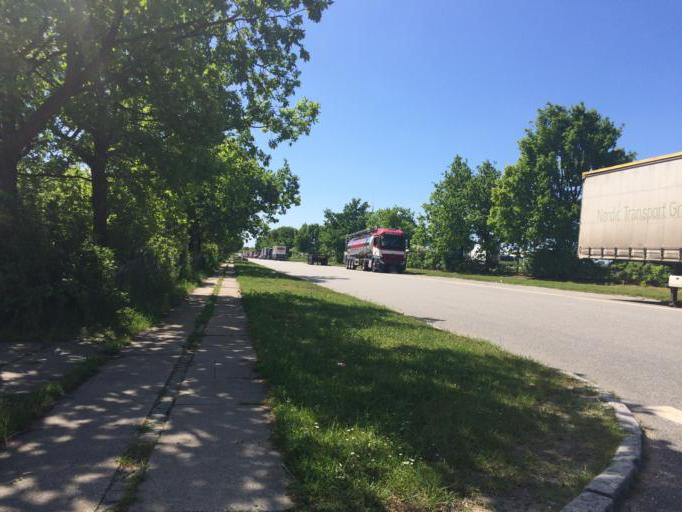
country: DK
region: Capital Region
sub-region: Hvidovre Kommune
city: Hvidovre
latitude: 55.6125
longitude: 12.4604
